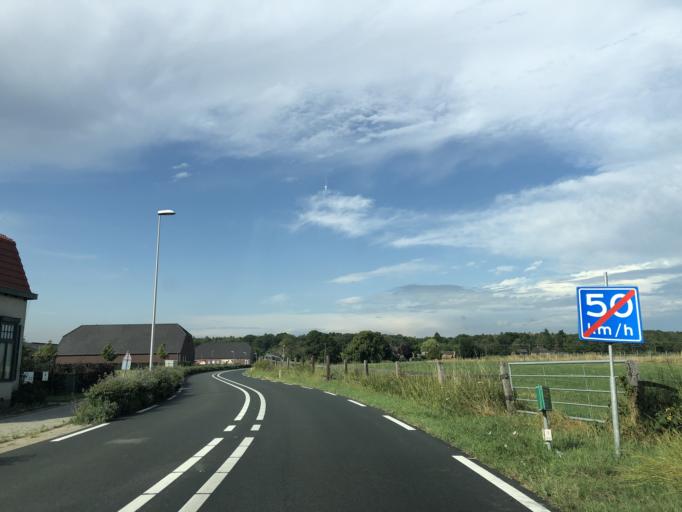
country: NL
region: Limburg
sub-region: Gemeente Gennep
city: Gennep
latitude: 51.7150
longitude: 6.0435
